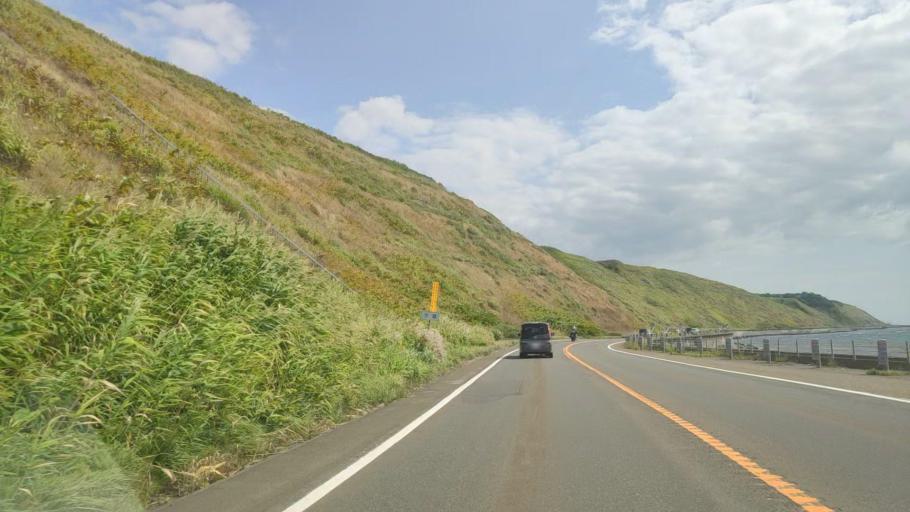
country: JP
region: Hokkaido
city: Rumoi
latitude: 44.2451
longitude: 141.6574
